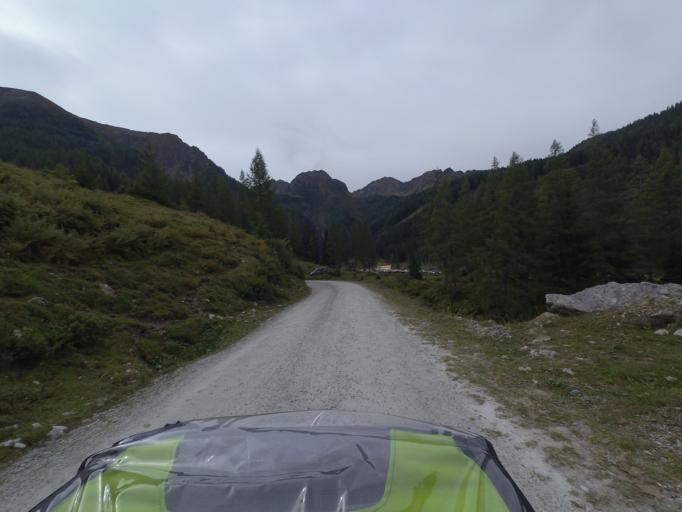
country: AT
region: Salzburg
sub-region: Politischer Bezirk Sankt Johann im Pongau
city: Untertauern
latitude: 47.2926
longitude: 13.5796
